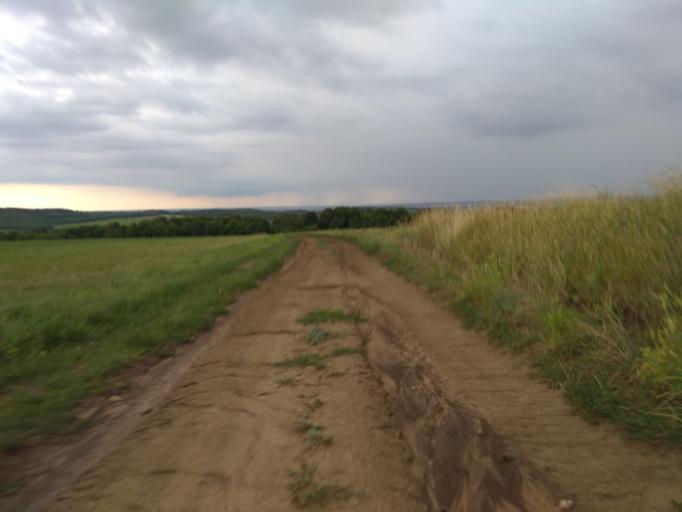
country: HU
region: Borsod-Abauj-Zemplen
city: Megyaszo
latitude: 48.1796
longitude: 21.0992
